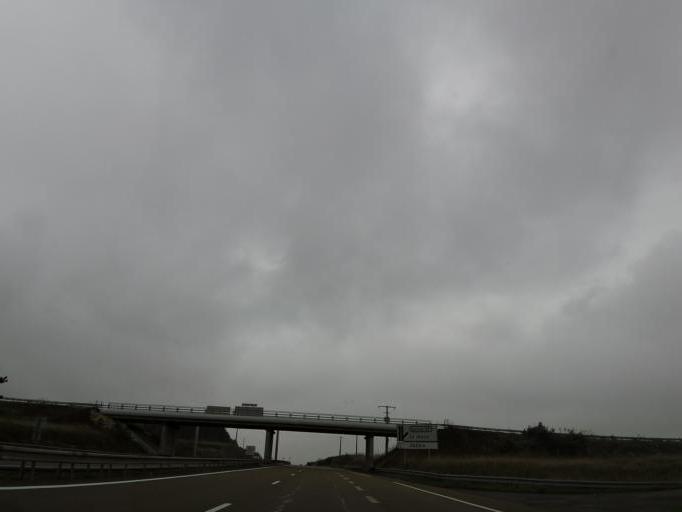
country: FR
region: Champagne-Ardenne
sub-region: Departement de la Marne
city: Fagnieres
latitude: 49.0517
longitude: 4.2928
